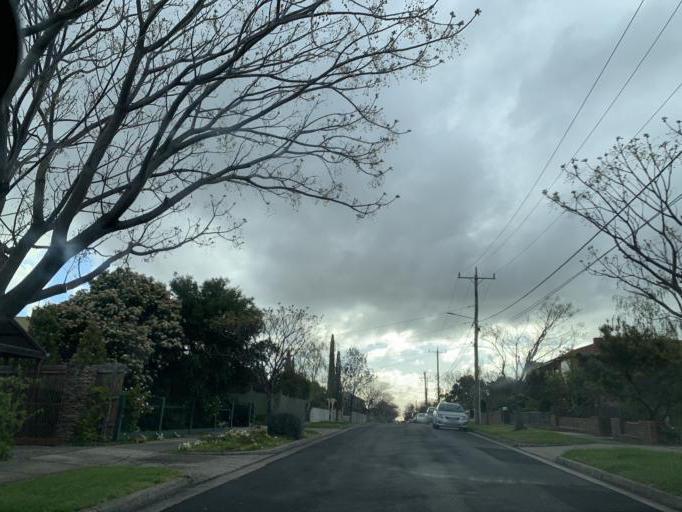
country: AU
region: Victoria
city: Thornbury
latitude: -37.7445
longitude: 144.9886
